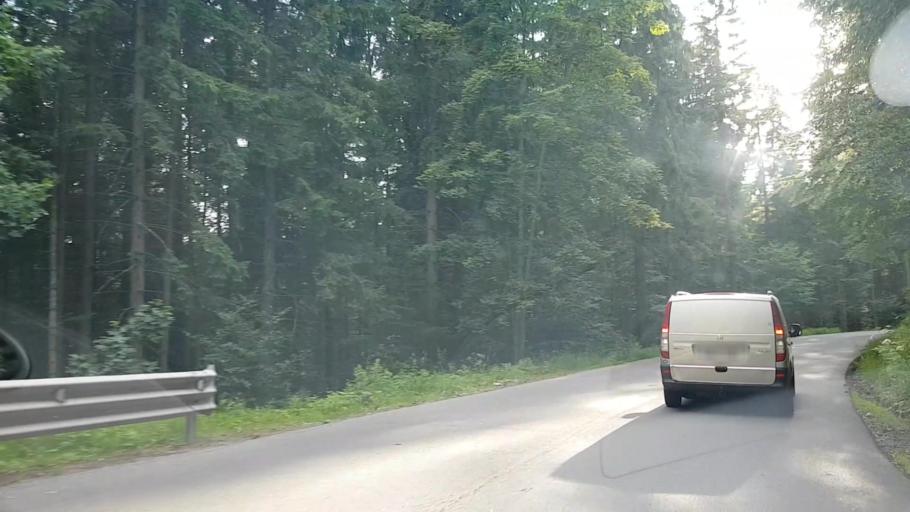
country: RO
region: Harghita
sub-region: Comuna Varsag
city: Varsag
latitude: 46.6689
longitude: 25.3318
